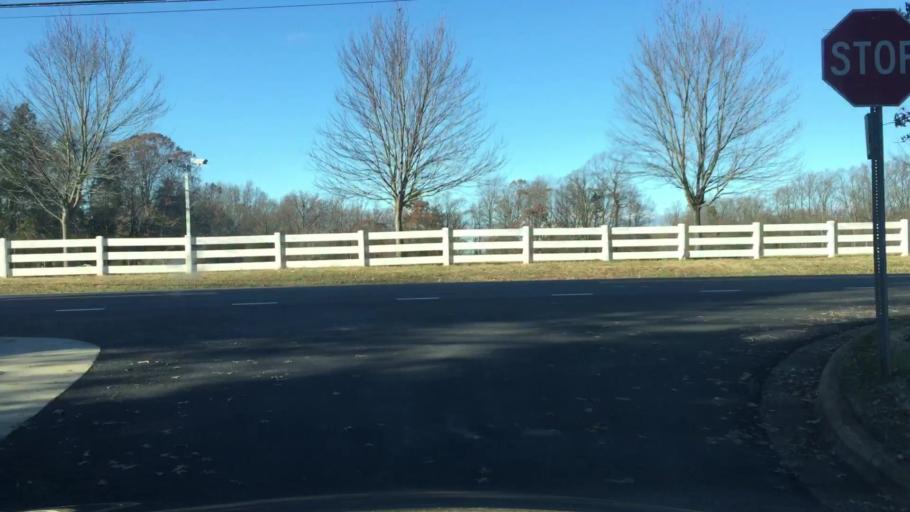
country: US
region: North Carolina
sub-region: Mecklenburg County
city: Cornelius
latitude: 35.5238
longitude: -80.8820
